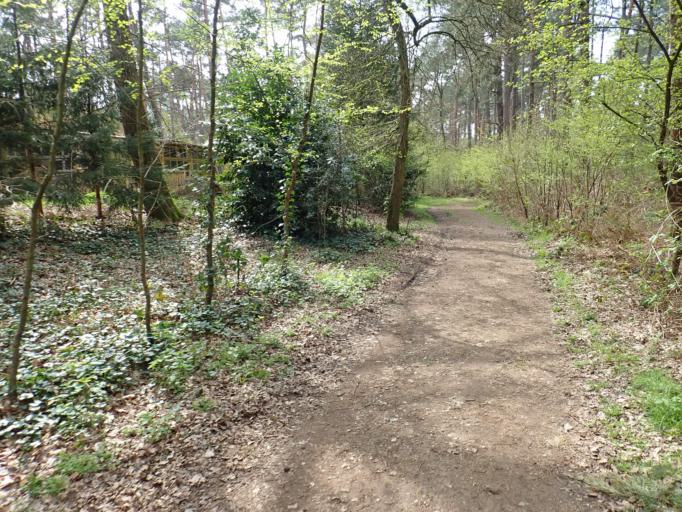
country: BE
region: Flanders
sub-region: Provincie Antwerpen
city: Kasterlee
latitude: 51.2278
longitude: 4.9435
